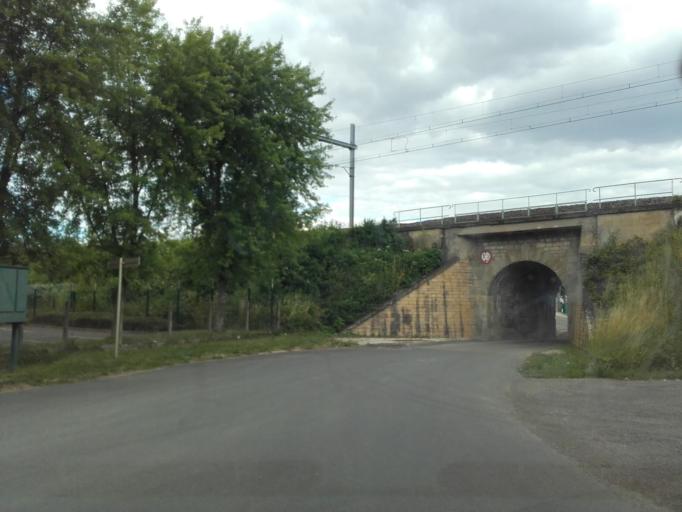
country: FR
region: Bourgogne
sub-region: Departement de Saone-et-Loire
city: Chagny
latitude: 46.9174
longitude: 4.7518
